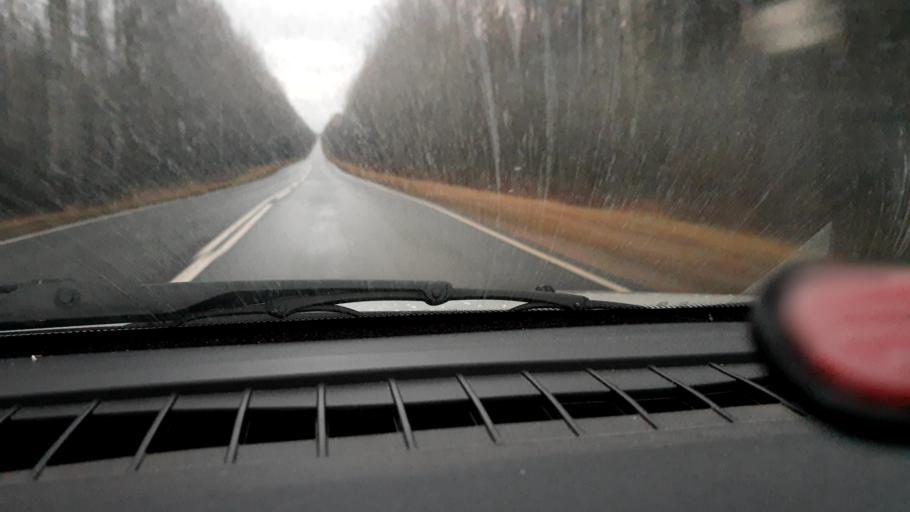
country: RU
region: Nizjnij Novgorod
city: Uren'
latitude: 57.2528
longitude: 45.6063
